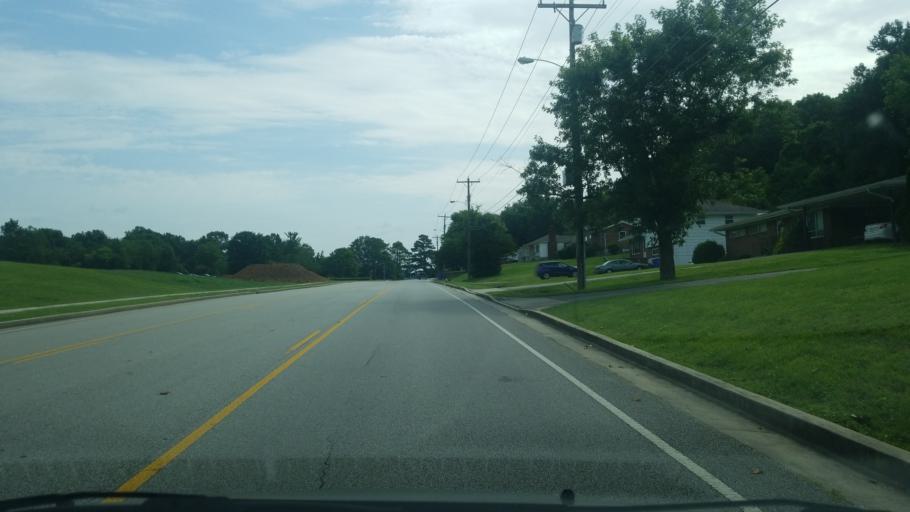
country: US
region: Tennessee
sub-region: Hamilton County
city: Collegedale
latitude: 35.0439
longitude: -85.0447
